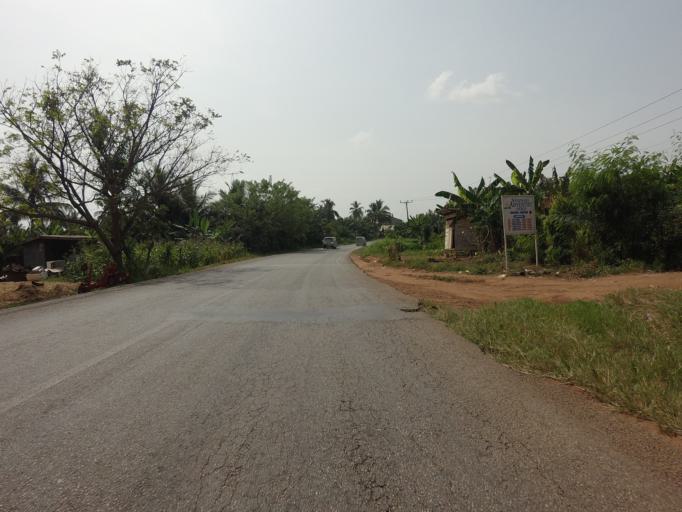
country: GH
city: Akropong
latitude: 6.2606
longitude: 0.1354
